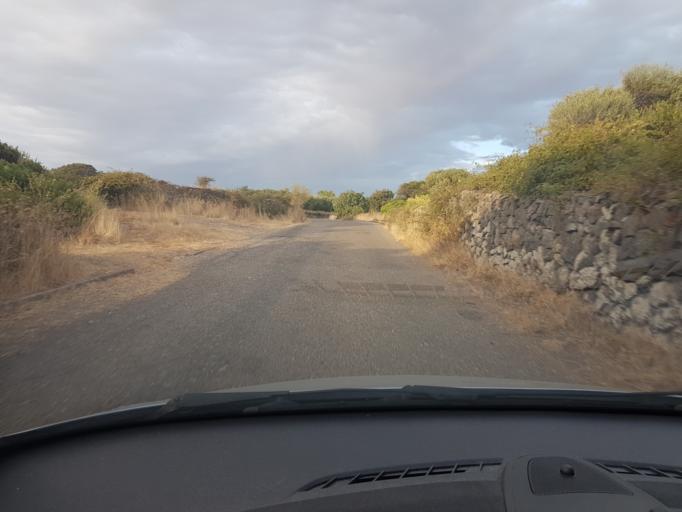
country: IT
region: Sardinia
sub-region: Provincia di Oristano
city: Seneghe
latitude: 40.0922
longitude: 8.6206
